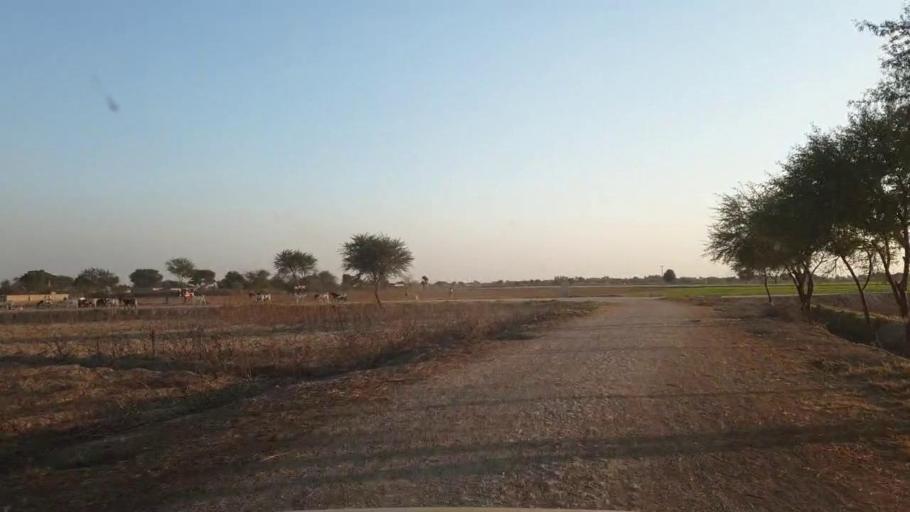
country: PK
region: Sindh
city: Chambar
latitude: 25.3149
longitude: 68.6552
